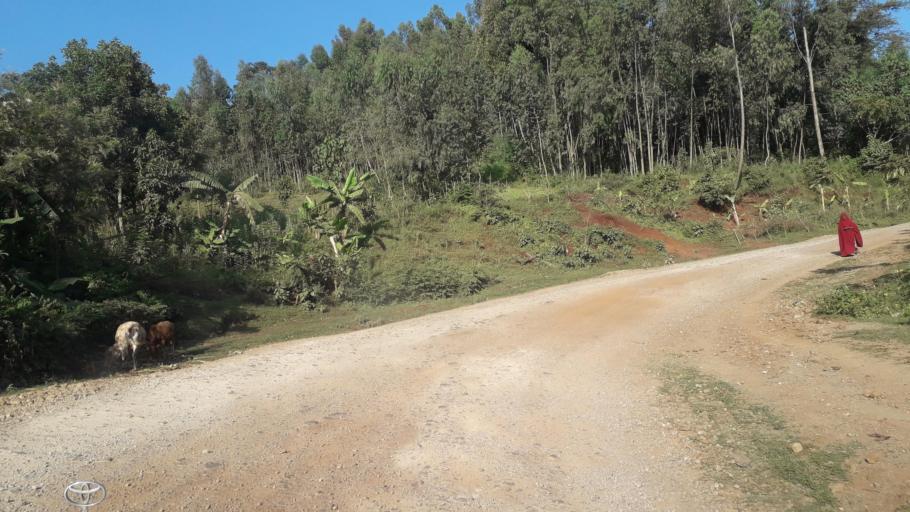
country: ET
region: Oromiya
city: Jima
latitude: 7.4856
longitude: 36.8760
